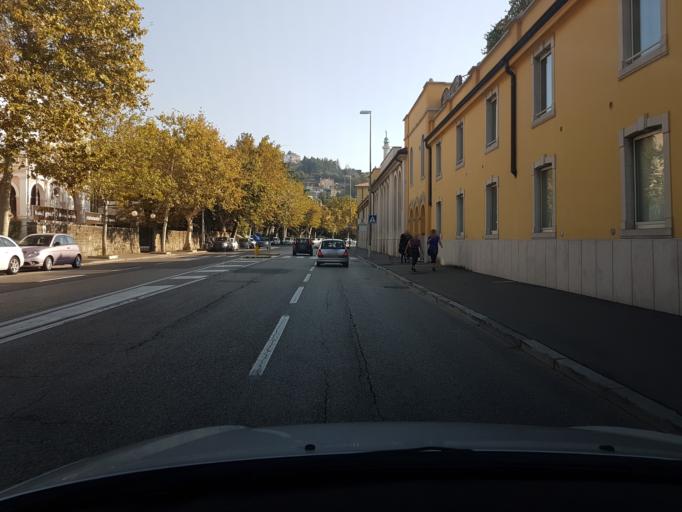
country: IT
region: Friuli Venezia Giulia
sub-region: Provincia di Trieste
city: Prosecco-Contovello
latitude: 45.6805
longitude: 13.7537
